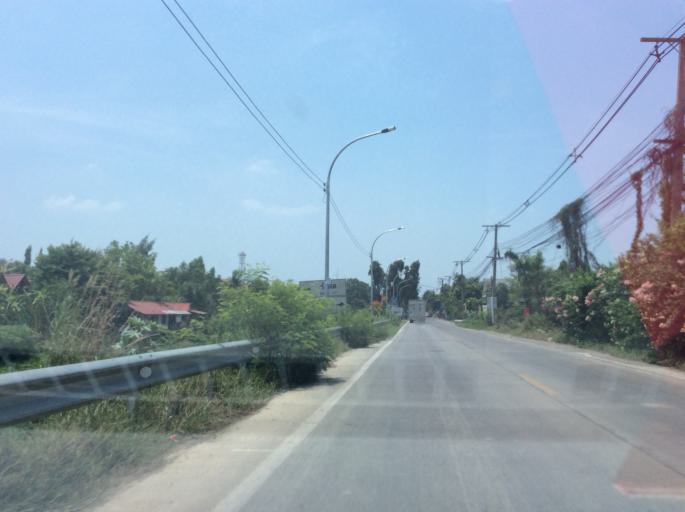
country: TH
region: Pathum Thani
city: Ban Rangsit
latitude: 14.0334
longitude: 100.7789
